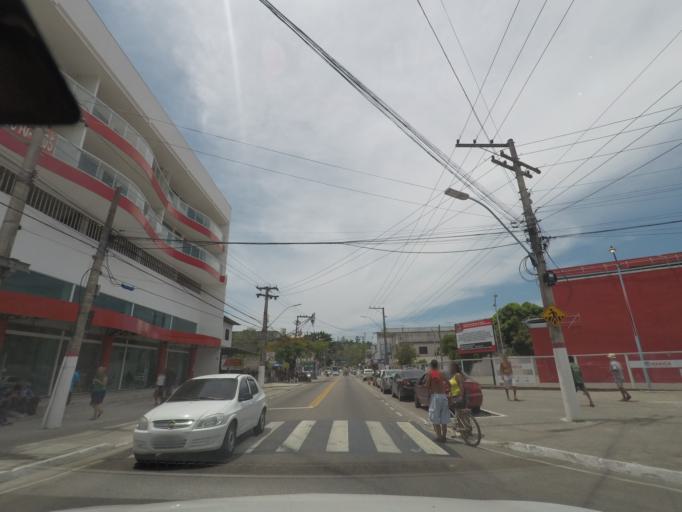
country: BR
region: Rio de Janeiro
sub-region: Marica
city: Marica
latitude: -22.9210
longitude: -42.8177
